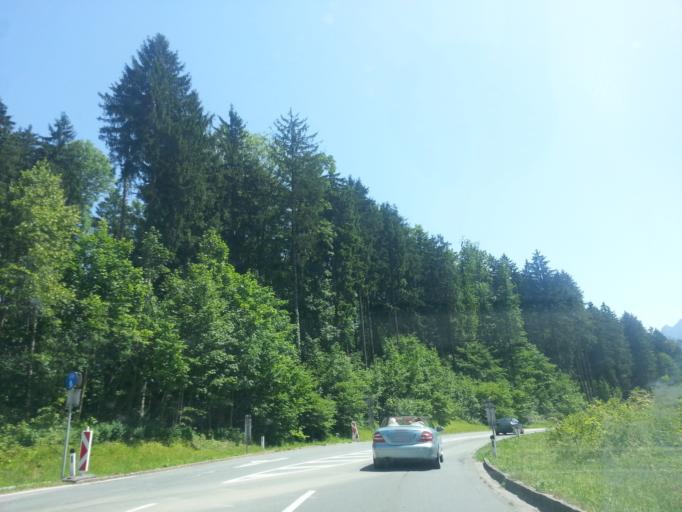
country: AT
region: Salzburg
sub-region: Politischer Bezirk Hallein
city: Adnet
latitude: 47.6640
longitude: 13.1243
